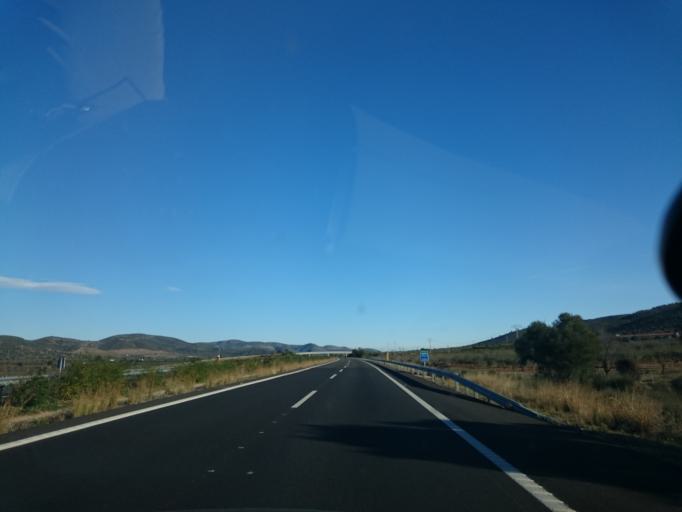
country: ES
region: Valencia
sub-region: Provincia de Castello
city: Alcala de Xivert
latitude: 40.3175
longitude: 0.2492
